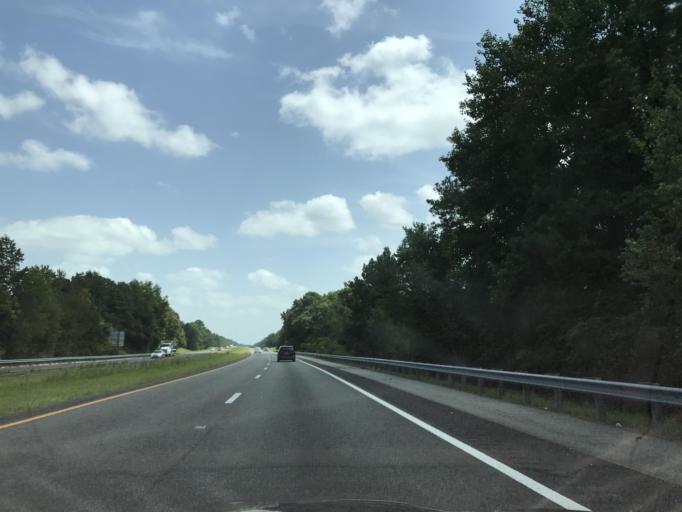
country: US
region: North Carolina
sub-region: Sampson County
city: Clinton
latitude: 35.2111
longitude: -78.3235
